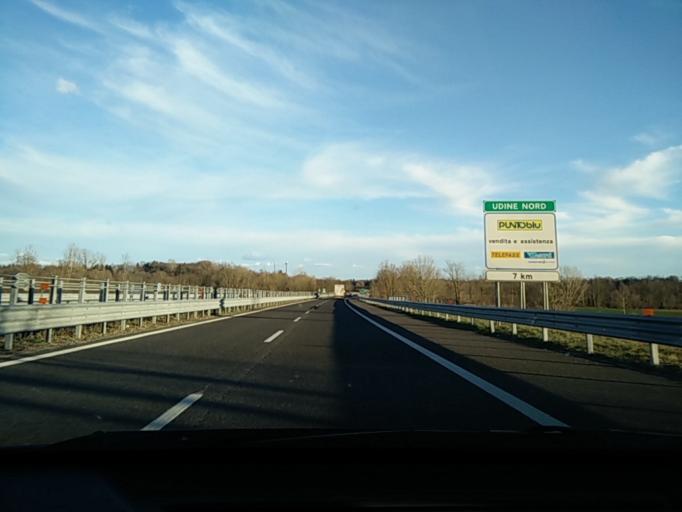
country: IT
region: Friuli Venezia Giulia
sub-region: Provincia di Udine
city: Collofedo di Monte Albano
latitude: 46.1655
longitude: 13.1577
